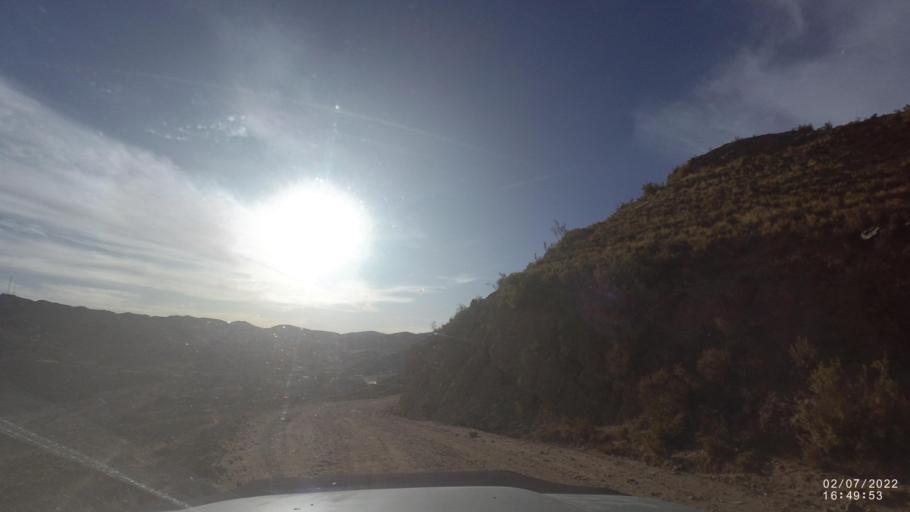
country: BO
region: Cochabamba
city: Irpa Irpa
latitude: -17.9749
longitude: -66.5285
